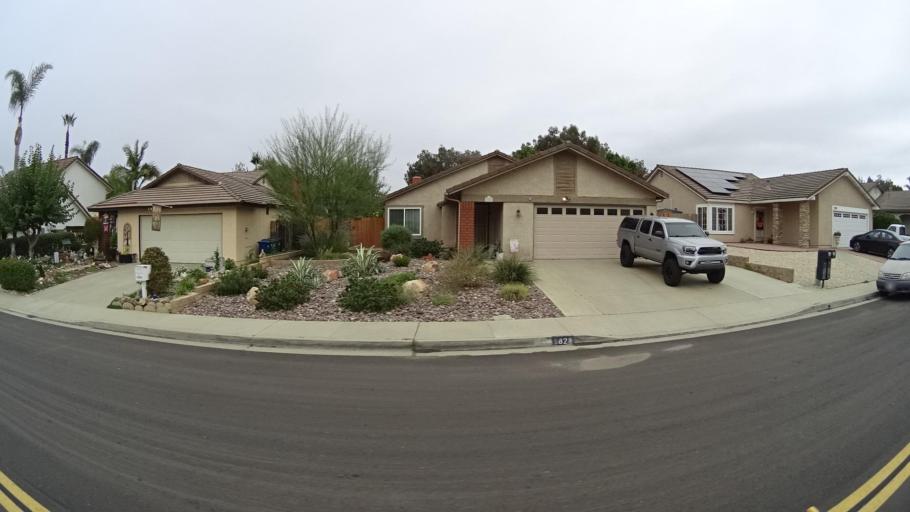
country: US
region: California
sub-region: San Diego County
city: Rancho San Diego
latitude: 32.7559
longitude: -116.9171
